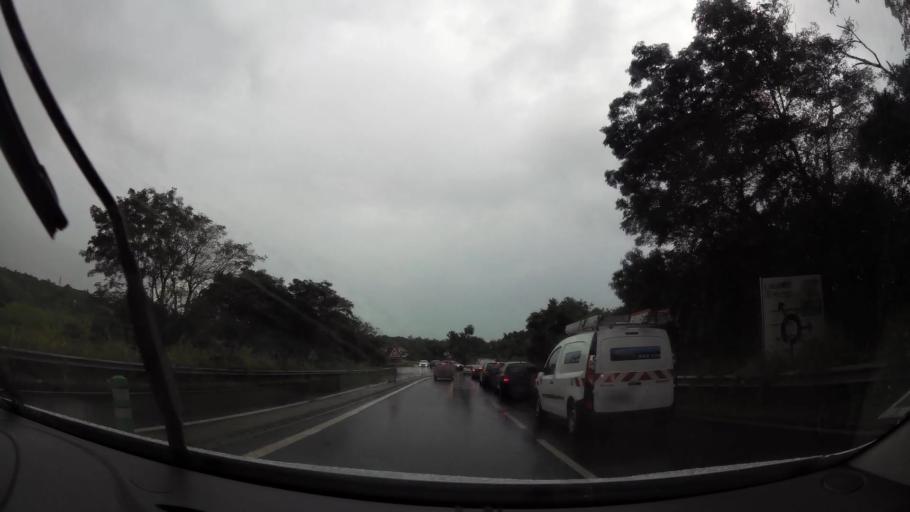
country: RE
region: Reunion
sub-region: Reunion
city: Saint-Benoit
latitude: -21.0270
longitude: 55.7049
